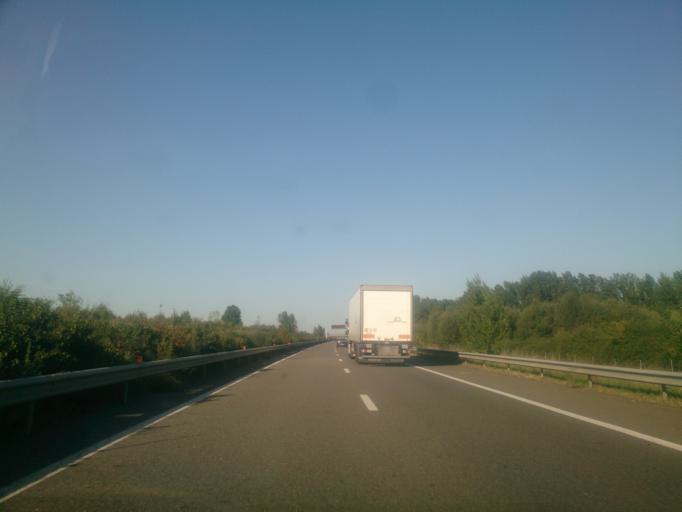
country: FR
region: Midi-Pyrenees
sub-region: Departement du Tarn-et-Garonne
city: Realville
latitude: 44.1303
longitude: 1.4843
